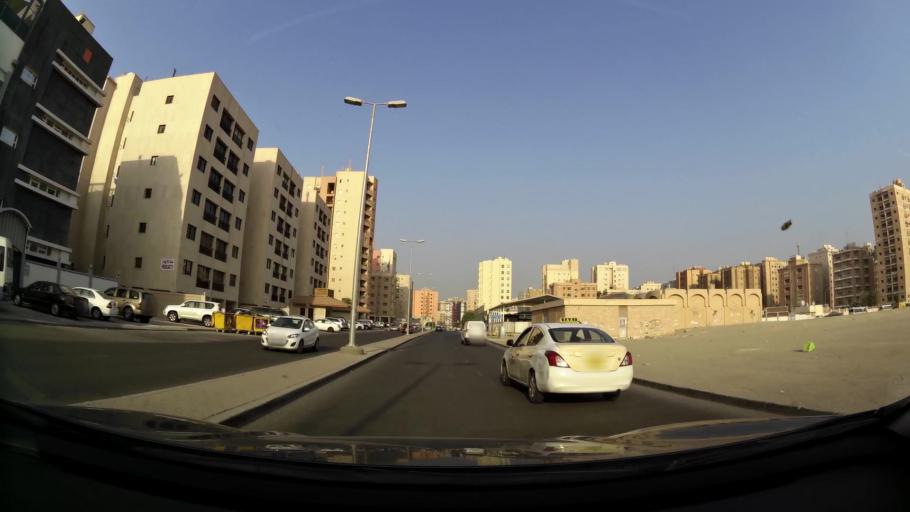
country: KW
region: Muhafazat Hawalli
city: Hawalli
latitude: 29.3283
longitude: 48.0497
